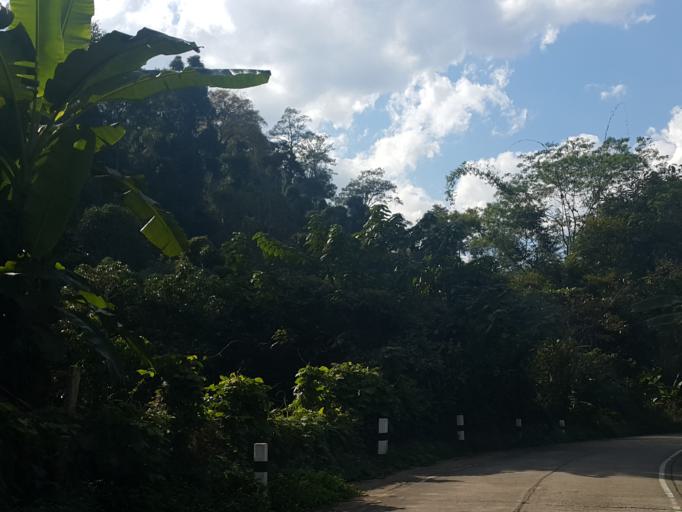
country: TH
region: Chiang Mai
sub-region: Amphoe Chiang Dao
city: Chiang Dao
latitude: 19.4127
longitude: 98.9194
